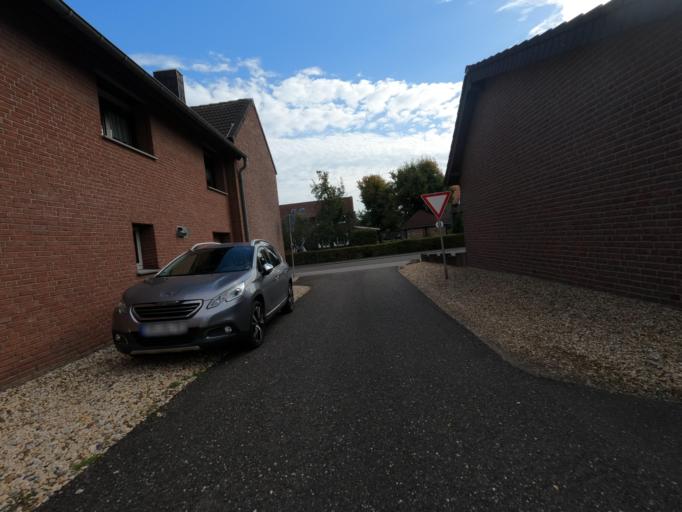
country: DE
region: North Rhine-Westphalia
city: Geilenkirchen
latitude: 50.9907
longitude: 6.0933
